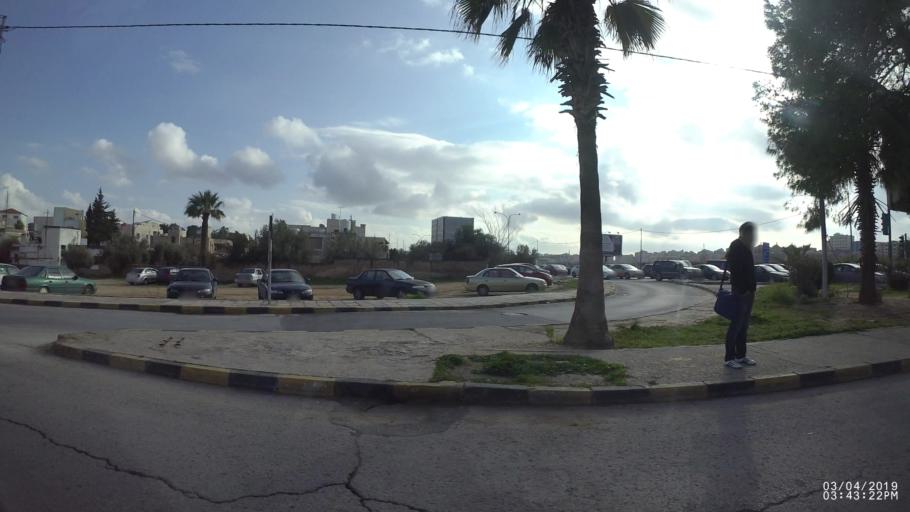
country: JO
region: Amman
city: Umm as Summaq
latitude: 31.9015
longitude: 35.8530
